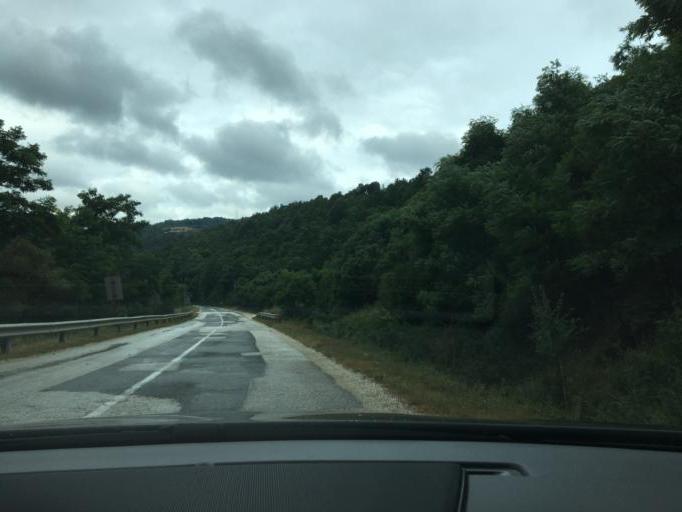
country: MK
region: Kriva Palanka
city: Kriva Palanka
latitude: 42.2234
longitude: 22.4216
